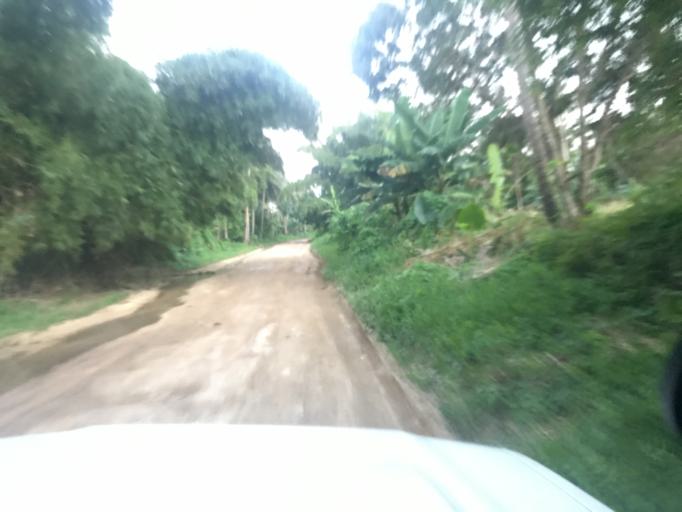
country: VU
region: Sanma
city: Luganville
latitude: -15.5539
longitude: 166.9933
